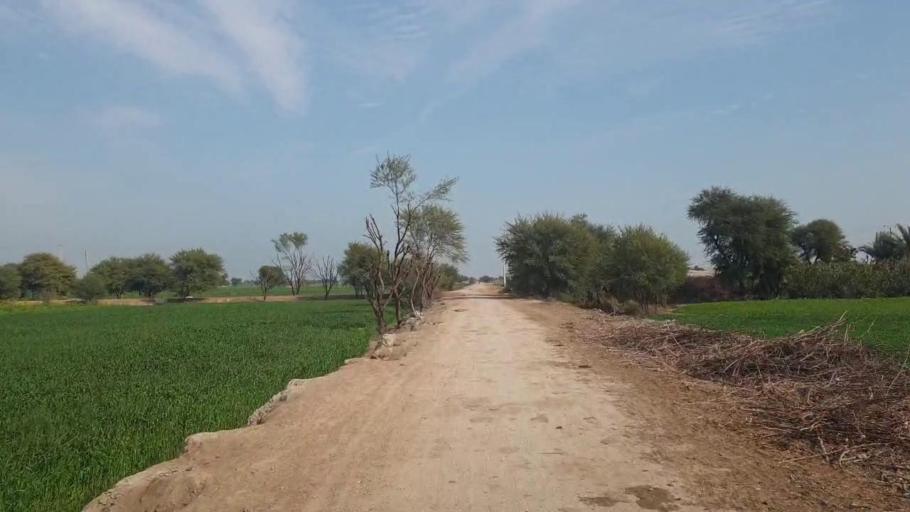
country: PK
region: Sindh
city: Shahdadpur
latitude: 26.0150
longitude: 68.5469
